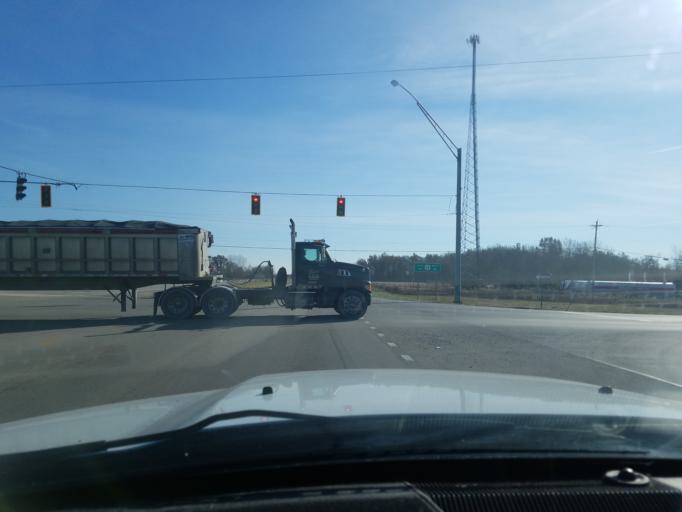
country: US
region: Ohio
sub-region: Adams County
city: Winchester
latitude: 38.9670
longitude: -83.7274
